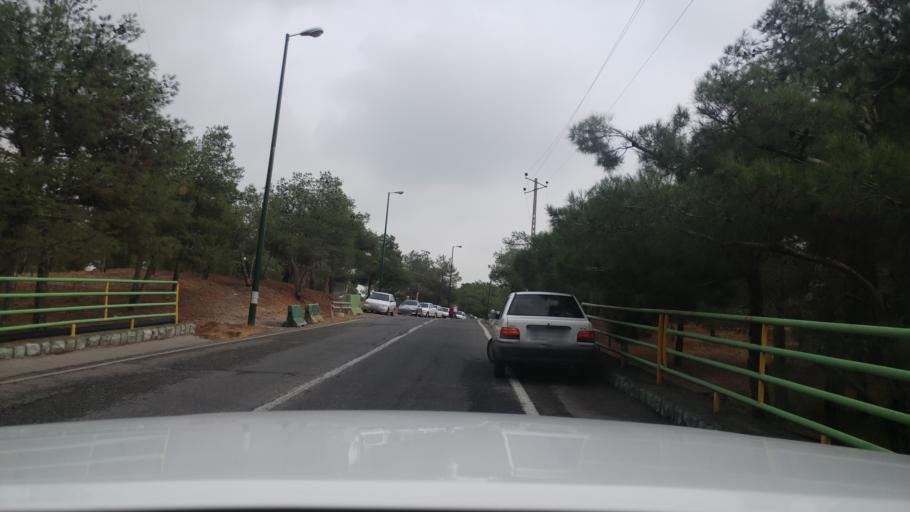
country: IR
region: Tehran
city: Shahr-e Qods
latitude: 35.7269
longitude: 51.2212
